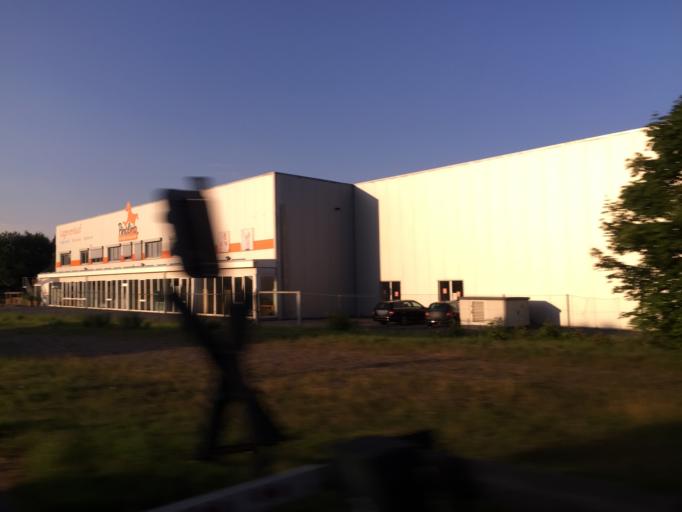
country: DE
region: North Rhine-Westphalia
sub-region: Regierungsbezirk Munster
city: Muenster
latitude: 52.0046
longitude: 7.6149
